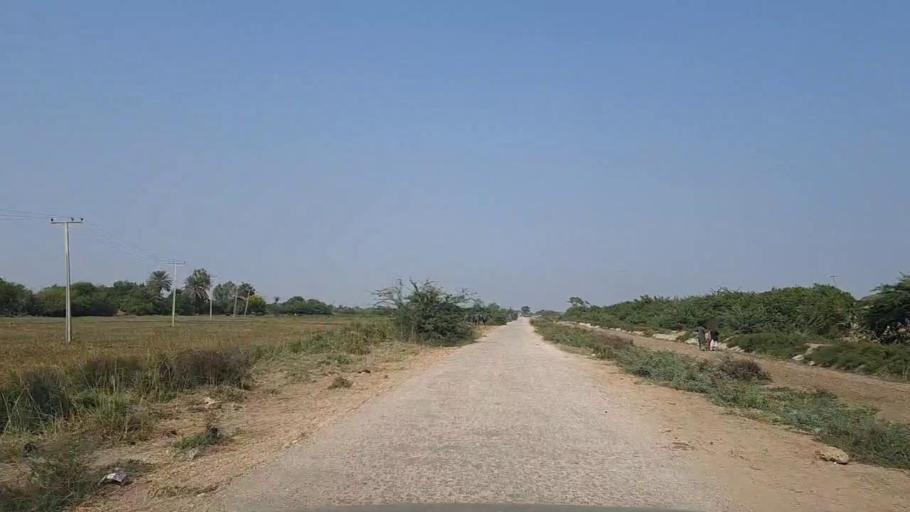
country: PK
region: Sindh
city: Chuhar Jamali
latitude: 24.5206
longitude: 67.9260
